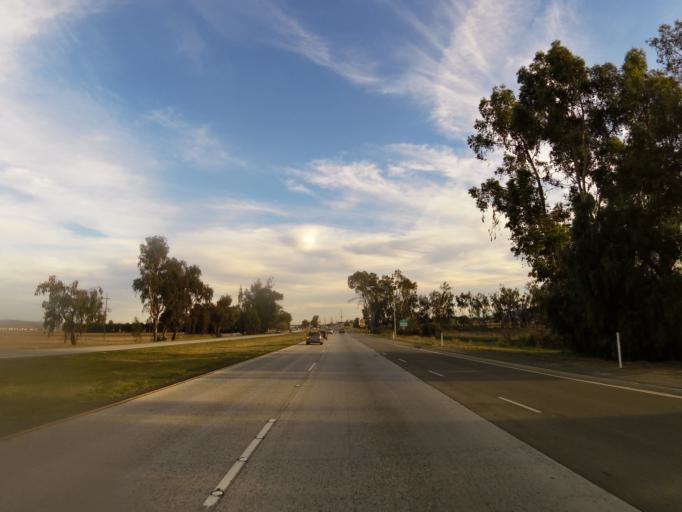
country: US
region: California
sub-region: Monterey County
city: Greenfield
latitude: 36.3375
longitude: -121.2533
